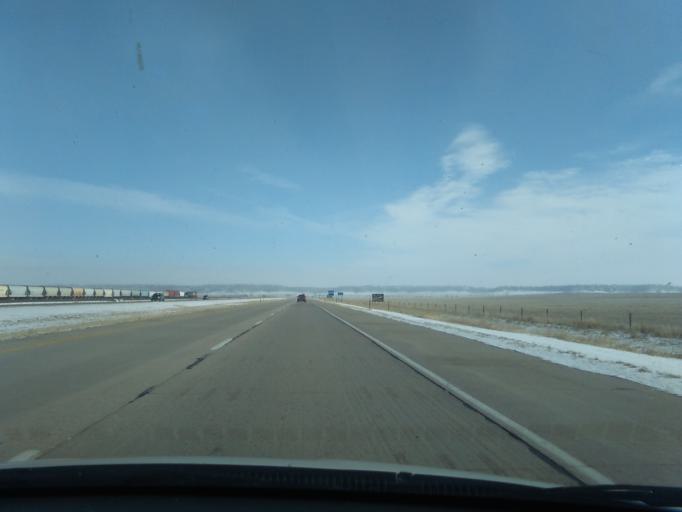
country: US
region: Wyoming
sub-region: Laramie County
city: Pine Bluffs
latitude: 41.1490
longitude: -104.1325
